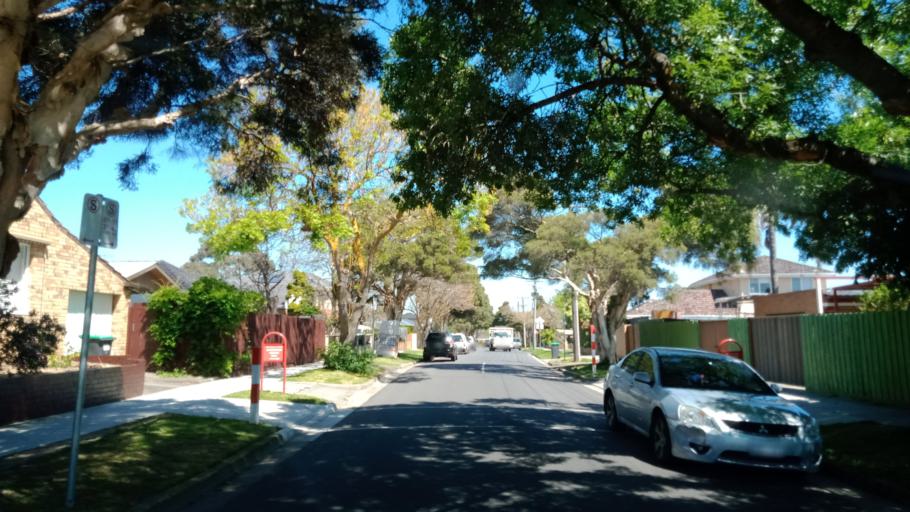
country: AU
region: Victoria
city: Murrumbeena
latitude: -37.9189
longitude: 145.0707
